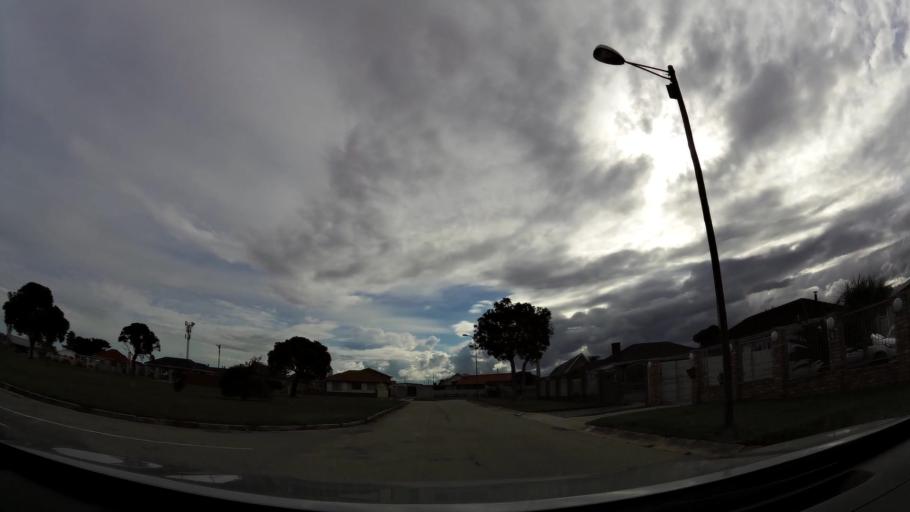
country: ZA
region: Eastern Cape
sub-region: Nelson Mandela Bay Metropolitan Municipality
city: Port Elizabeth
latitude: -33.9439
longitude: 25.4962
